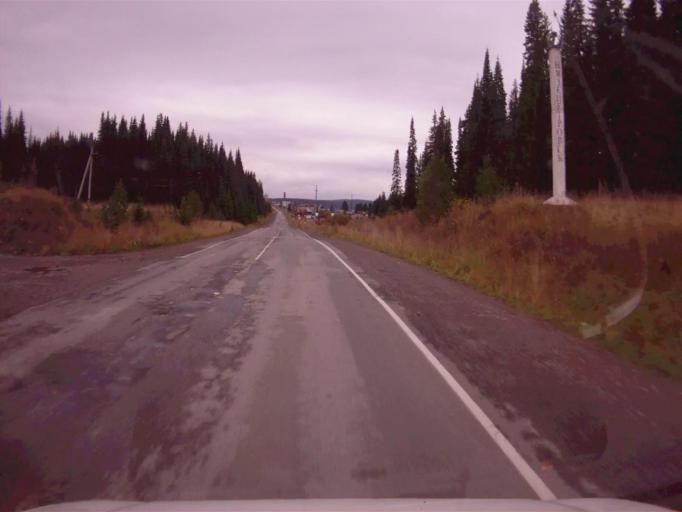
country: RU
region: Chelyabinsk
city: Nyazepetrovsk
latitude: 56.0661
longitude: 59.6332
